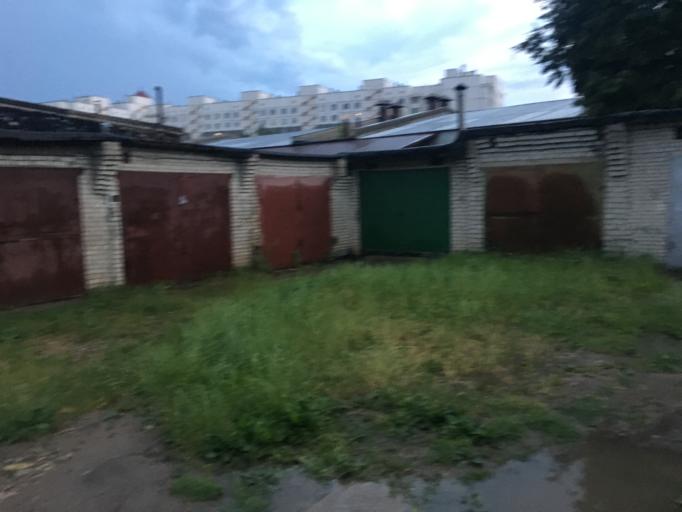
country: BY
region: Grodnenskaya
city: Hrodna
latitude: 53.6987
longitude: 23.8291
